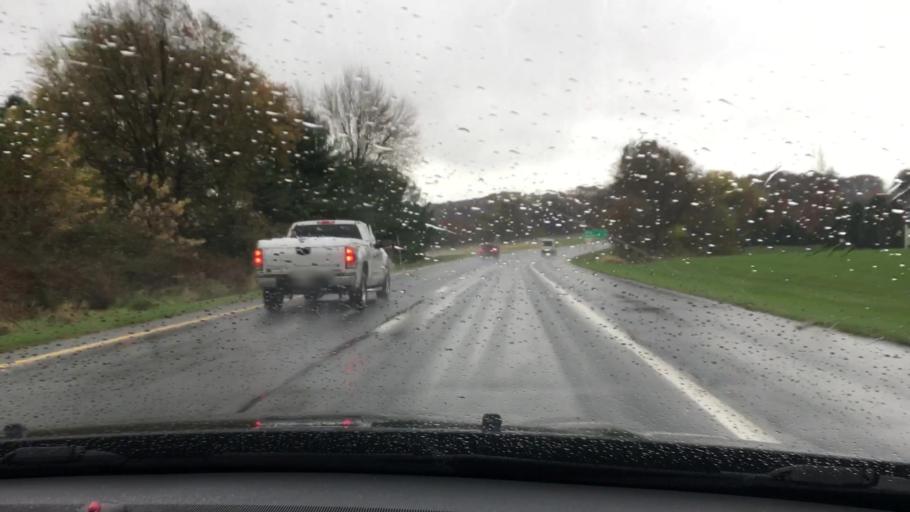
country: US
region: Pennsylvania
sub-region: Lancaster County
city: Willow Street
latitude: 39.9653
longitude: -76.2721
